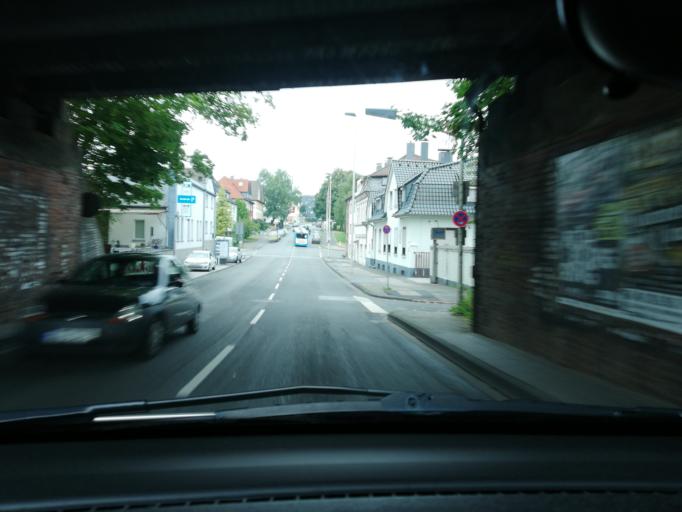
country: DE
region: North Rhine-Westphalia
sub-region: Regierungsbezirk Dusseldorf
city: Solingen
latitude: 51.1791
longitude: 7.0876
